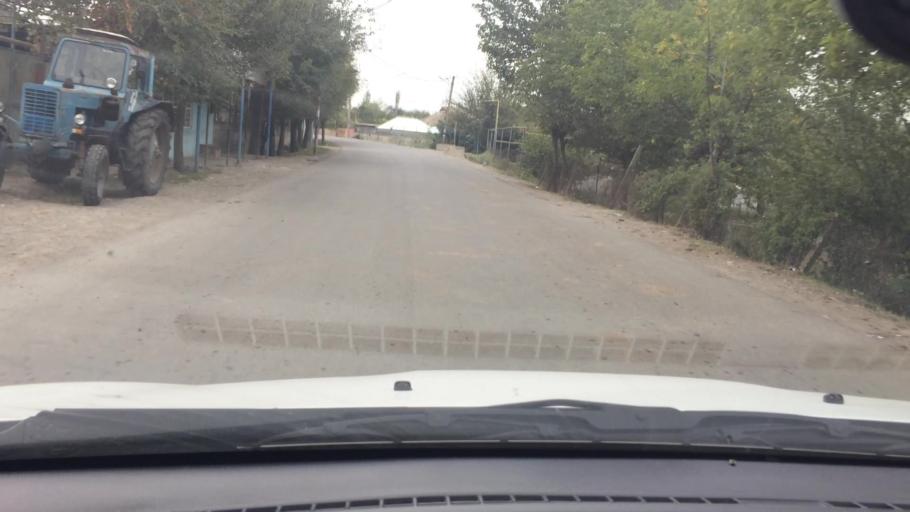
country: AM
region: Tavush
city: Berdavan
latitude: 41.3533
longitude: 44.9659
